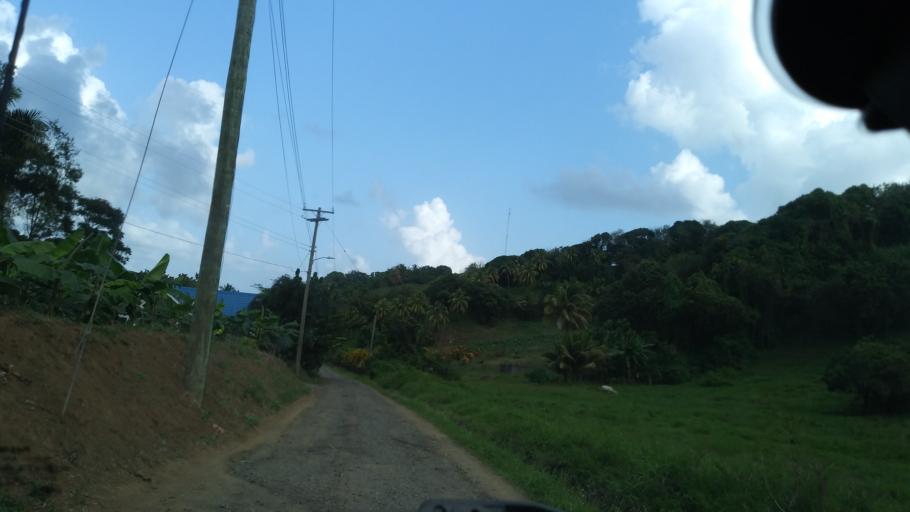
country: VC
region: Charlotte
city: Byera Village
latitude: 13.2316
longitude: -61.1326
